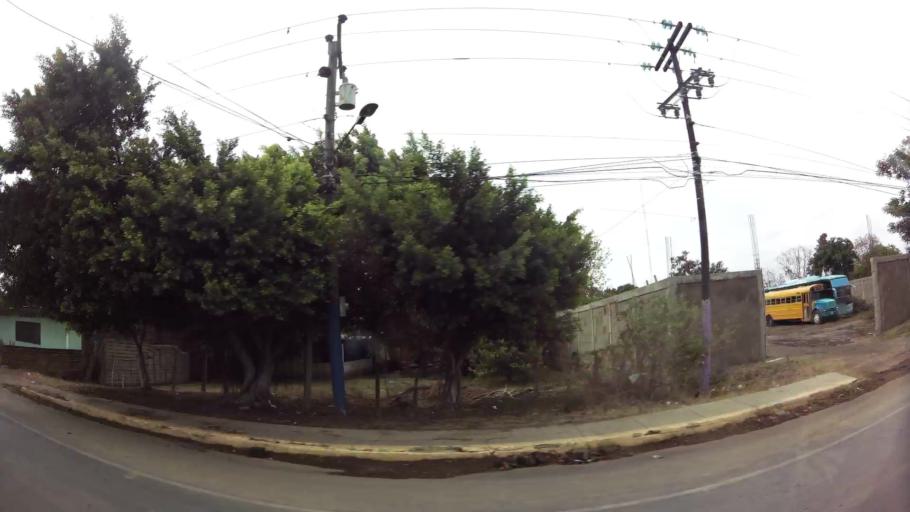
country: NI
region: Rivas
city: Rivas
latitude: 11.4490
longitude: -85.8184
